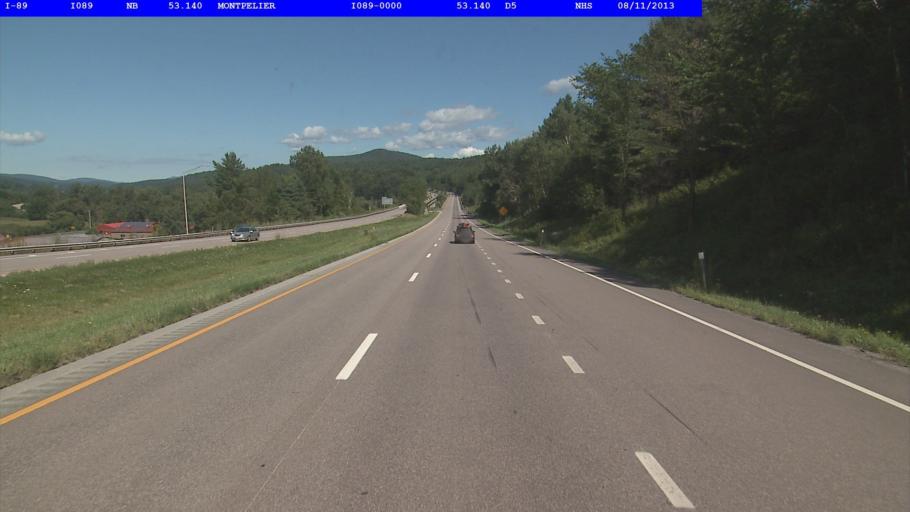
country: US
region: Vermont
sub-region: Washington County
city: Montpelier
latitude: 44.2532
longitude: -72.5979
